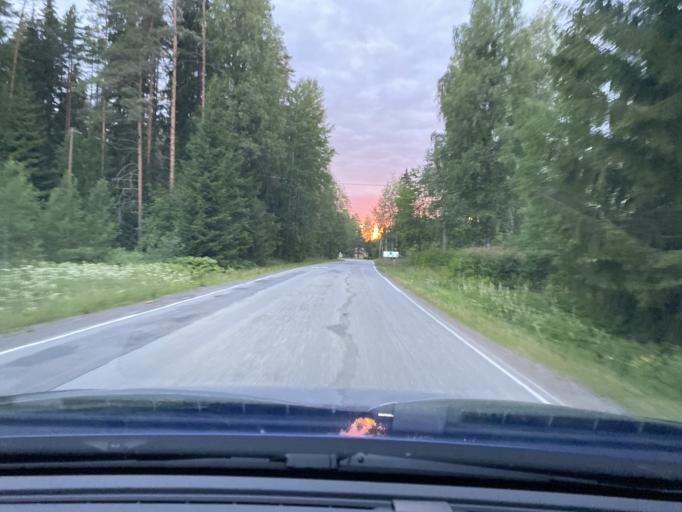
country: FI
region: Haeme
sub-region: Forssa
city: Tammela
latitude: 60.9723
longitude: 23.7017
